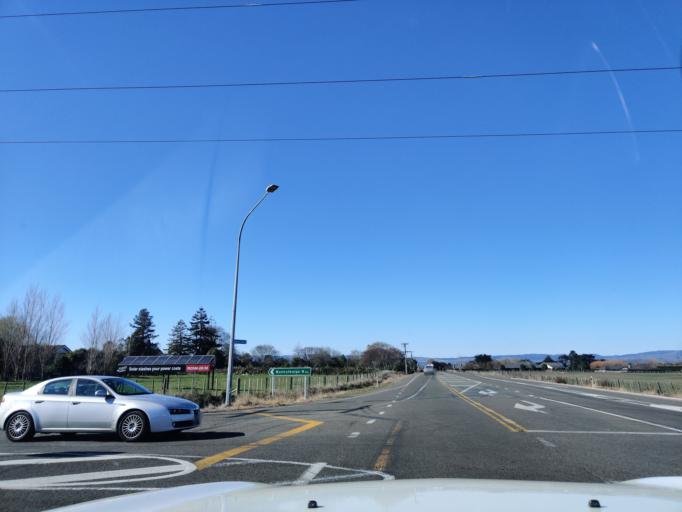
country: NZ
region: Manawatu-Wanganui
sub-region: Palmerston North City
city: Palmerston North
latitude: -40.3091
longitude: 175.5892
